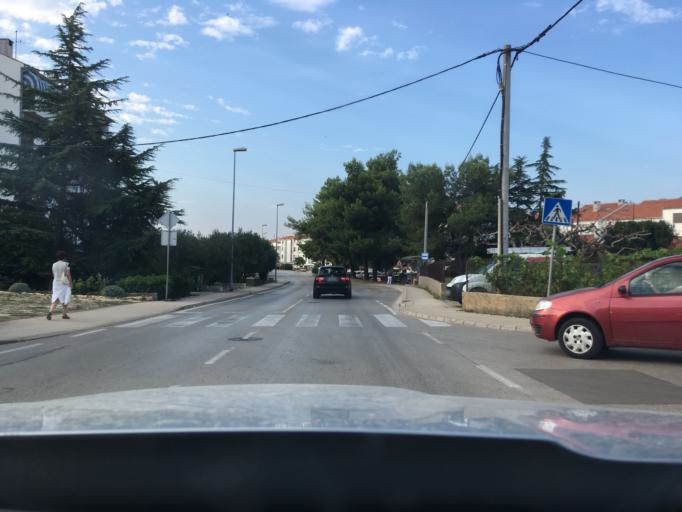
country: HR
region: Zadarska
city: Zadar
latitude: 44.1312
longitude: 15.2307
